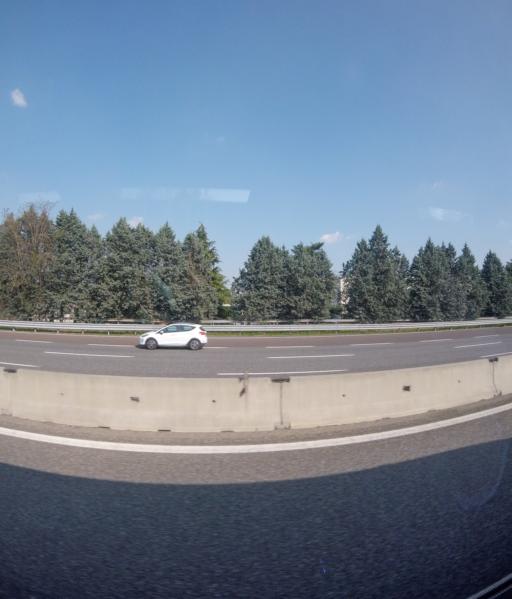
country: IT
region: Lombardy
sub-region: Provincia di Varese
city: Gallarate
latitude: 45.6695
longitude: 8.7996
